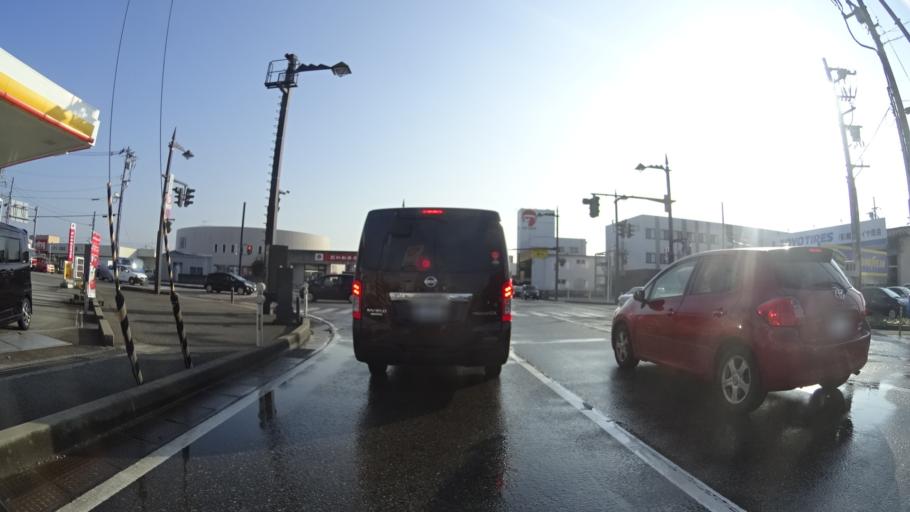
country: JP
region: Toyama
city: Toyama-shi
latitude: 36.7031
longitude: 137.2591
